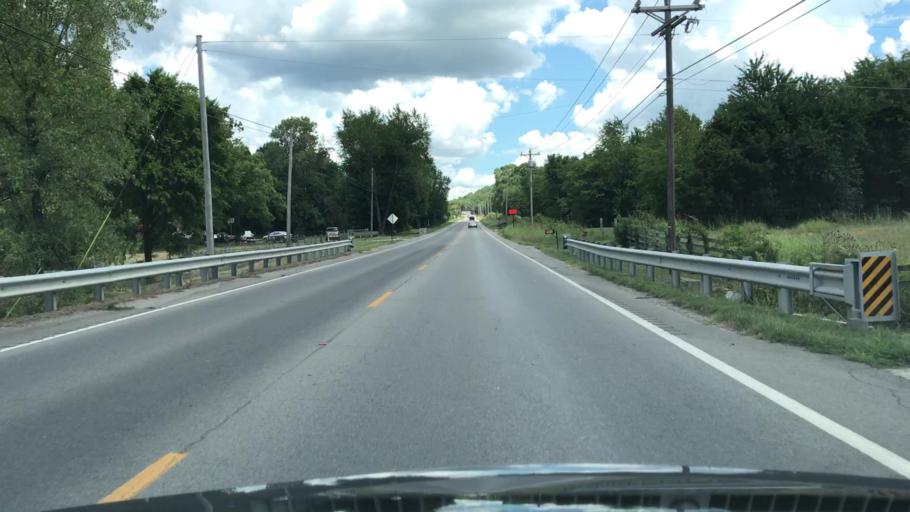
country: US
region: Tennessee
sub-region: Williamson County
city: Nolensville
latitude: 35.9110
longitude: -86.6618
